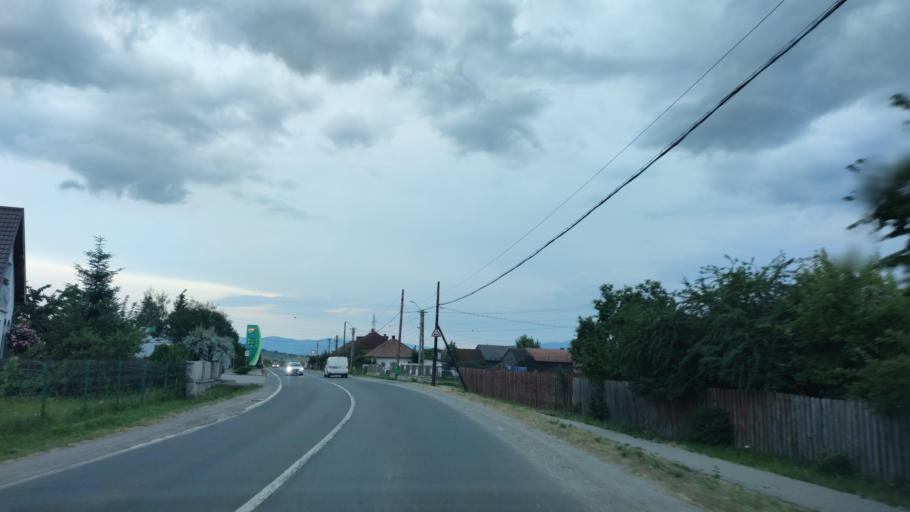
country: RO
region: Harghita
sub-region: Municipiul Gheorgheni
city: Gheorgheni
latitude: 46.7155
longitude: 25.6023
